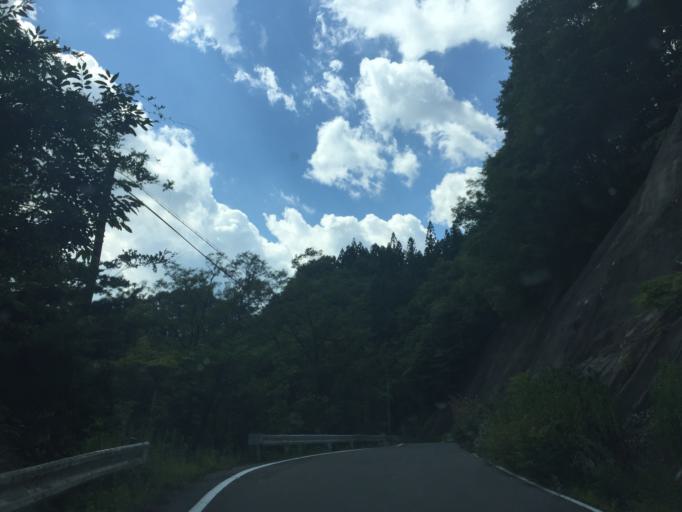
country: JP
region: Nagano
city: Iida
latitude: 35.3734
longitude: 137.7009
